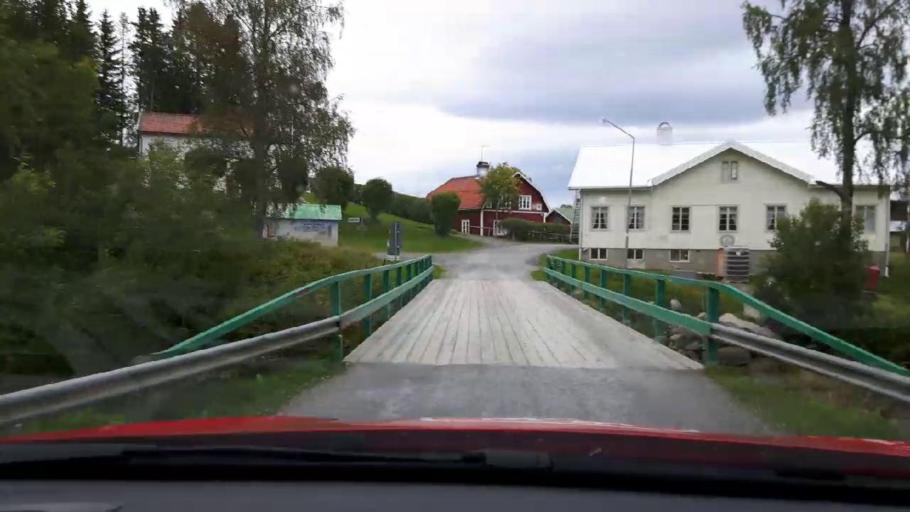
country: SE
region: Jaemtland
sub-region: Are Kommun
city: Are
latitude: 63.4903
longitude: 13.1210
